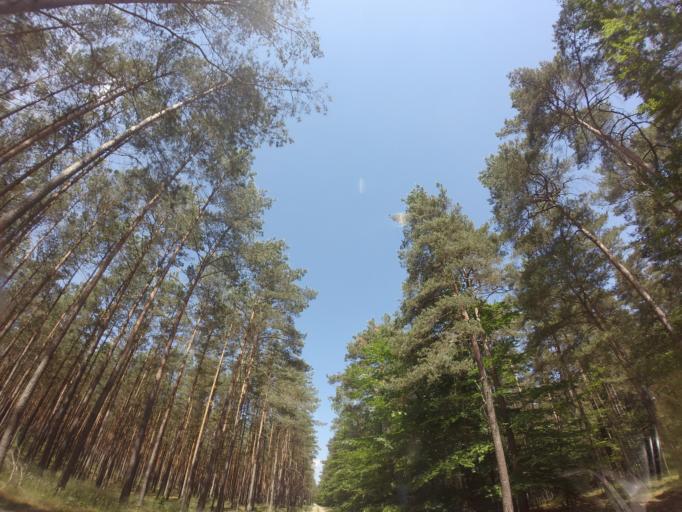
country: PL
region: West Pomeranian Voivodeship
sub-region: Powiat choszczenski
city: Drawno
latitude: 53.1534
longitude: 15.8063
